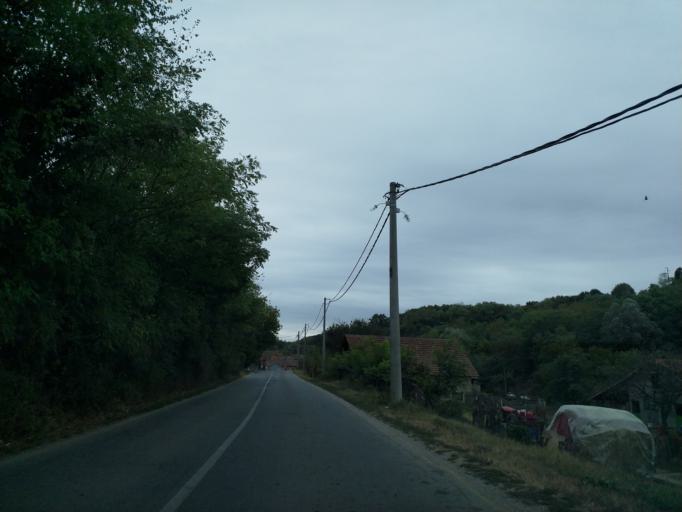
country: RS
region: Central Serbia
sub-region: Pomoravski Okrug
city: Jagodina
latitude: 44.0416
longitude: 21.1863
